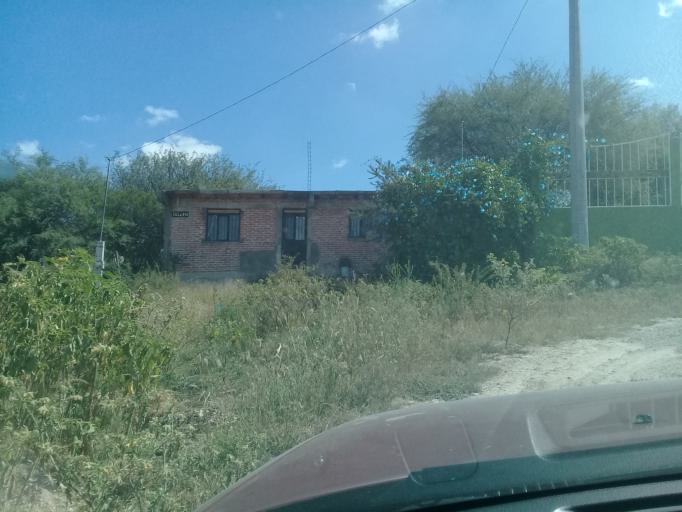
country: MX
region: Aguascalientes
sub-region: Aguascalientes
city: San Sebastian [Fraccionamiento]
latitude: 21.7802
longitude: -102.2591
